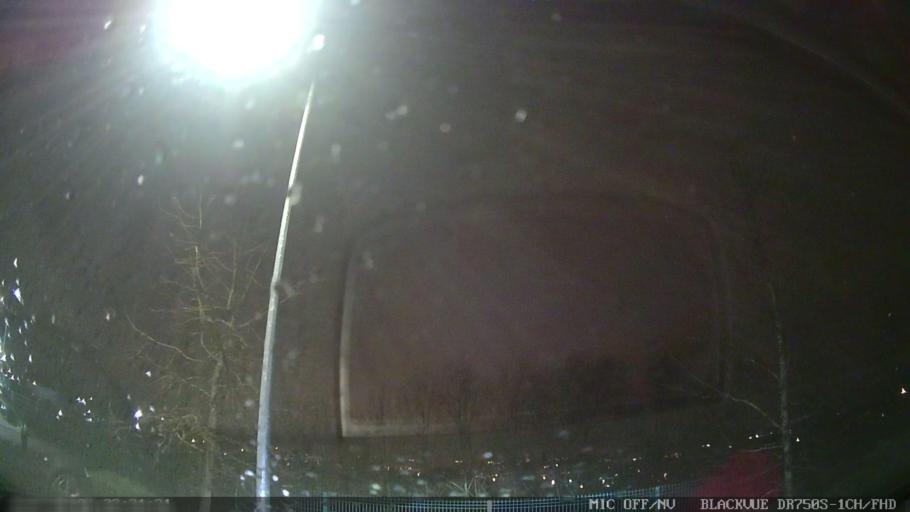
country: PT
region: Porto
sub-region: Penafiel
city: Penafiel
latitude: 41.1945
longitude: -8.3012
